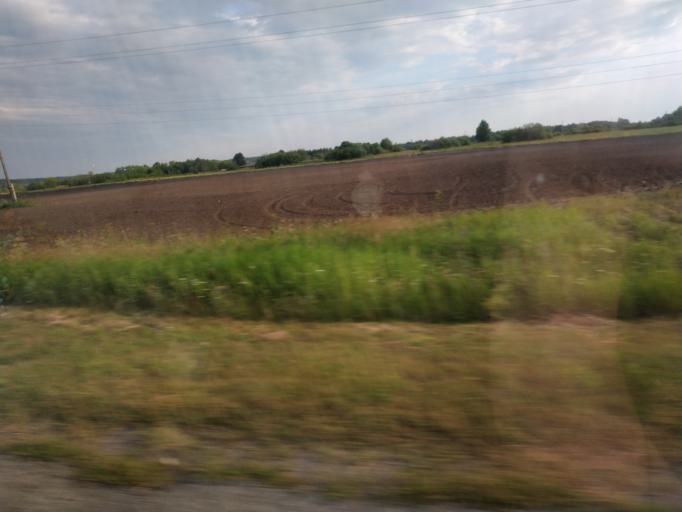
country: RU
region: Sverdlovsk
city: Kamyshlov
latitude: 57.0170
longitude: 62.7007
